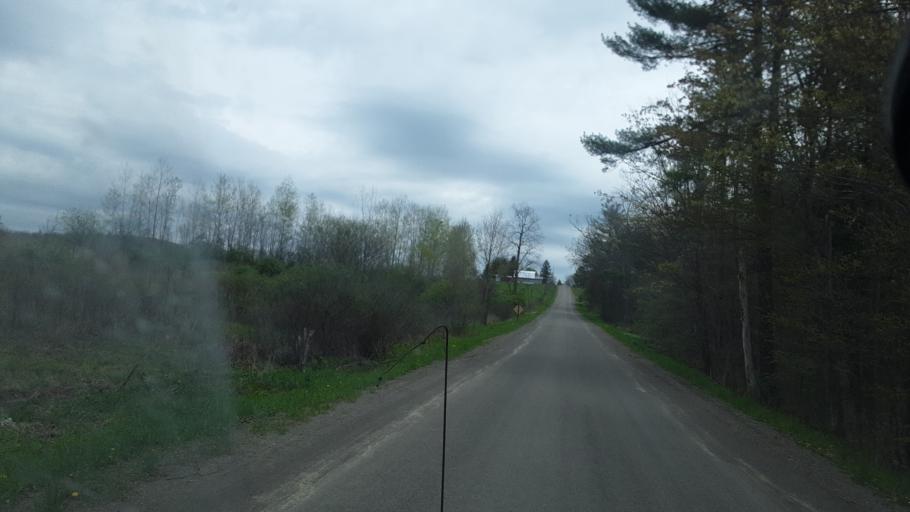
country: US
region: New York
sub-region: Steuben County
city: Addison
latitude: 42.0927
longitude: -77.2971
